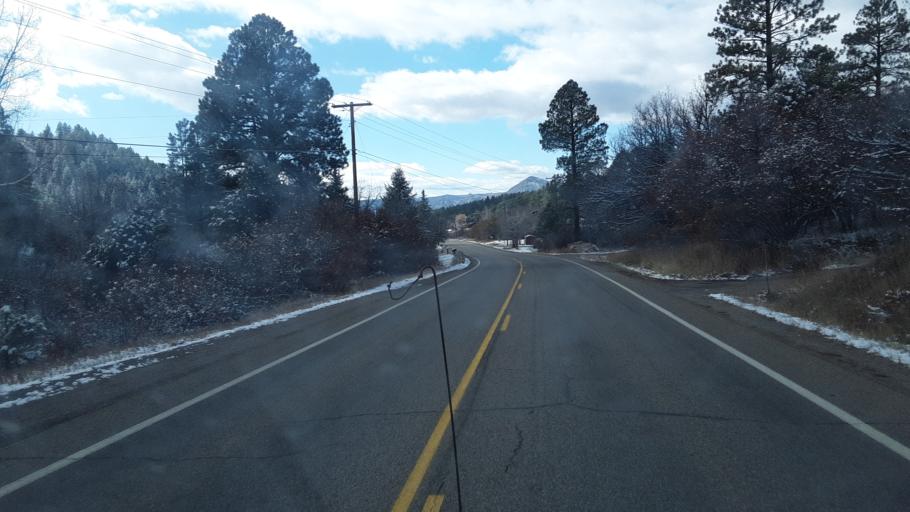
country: US
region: Colorado
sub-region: La Plata County
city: Durango
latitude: 37.3125
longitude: -107.8054
